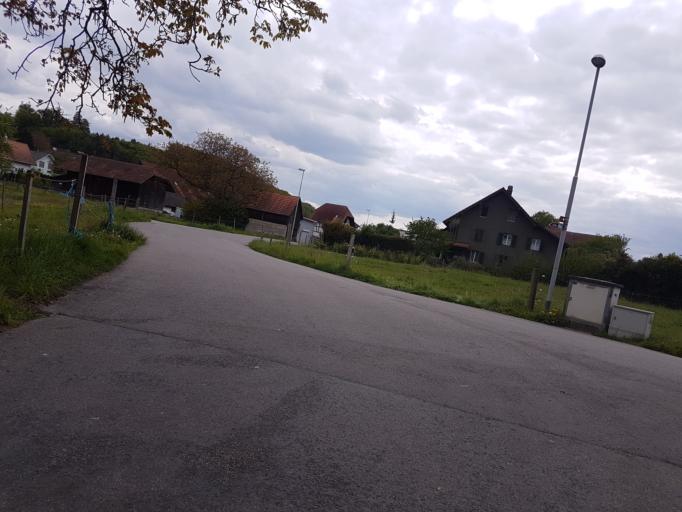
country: CH
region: Bern
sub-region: Seeland District
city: Arch
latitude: 47.1678
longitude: 7.4328
